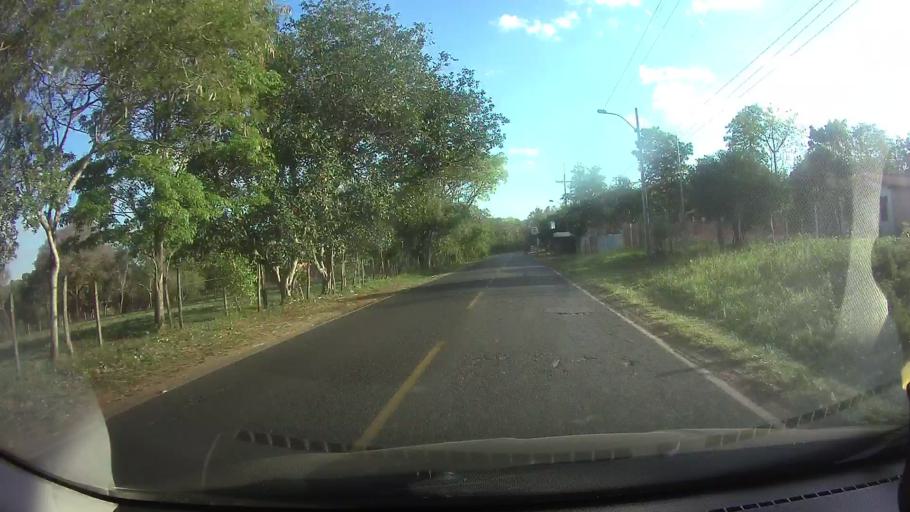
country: PY
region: Cordillera
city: Emboscada
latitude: -25.1938
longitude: -57.3190
